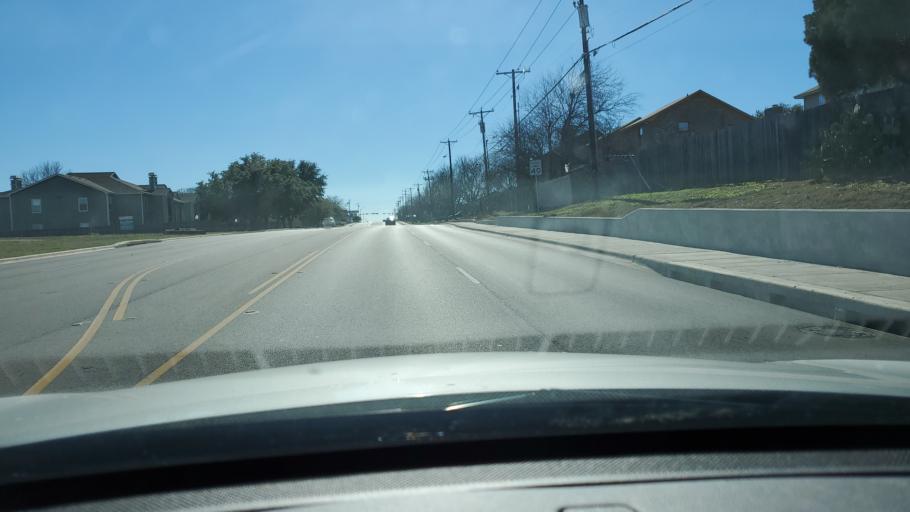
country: US
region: Texas
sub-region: Bell County
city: Killeen
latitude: 31.0894
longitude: -97.7344
